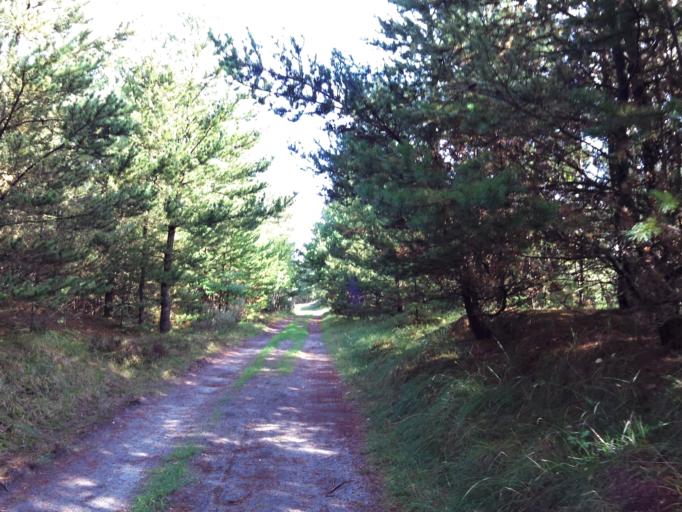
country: DK
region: South Denmark
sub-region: Varde Kommune
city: Oksbol
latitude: 55.5528
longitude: 8.2091
